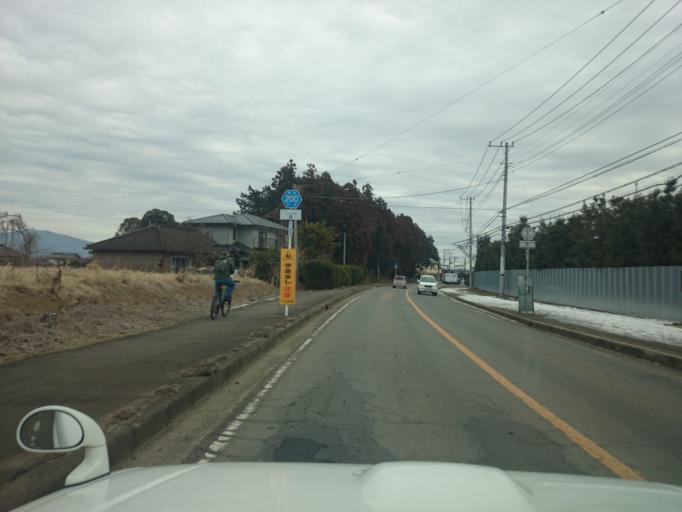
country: JP
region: Ibaraki
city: Tsukuba
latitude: 36.1124
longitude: 140.0775
